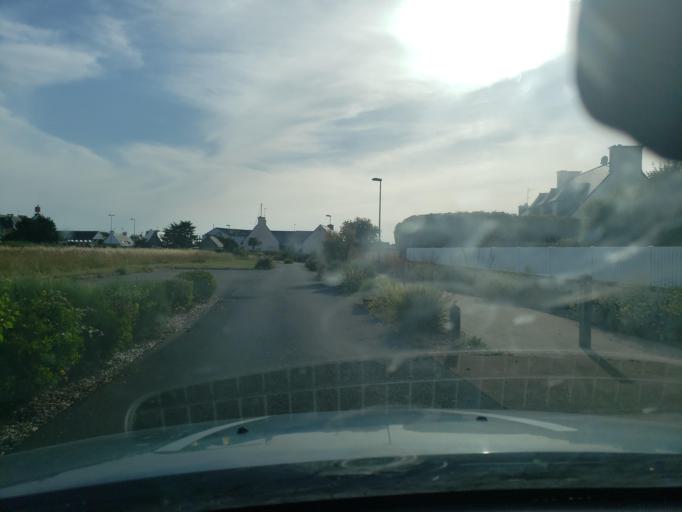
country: FR
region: Brittany
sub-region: Departement du Finistere
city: Guilvinec
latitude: 47.7984
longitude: -4.2689
